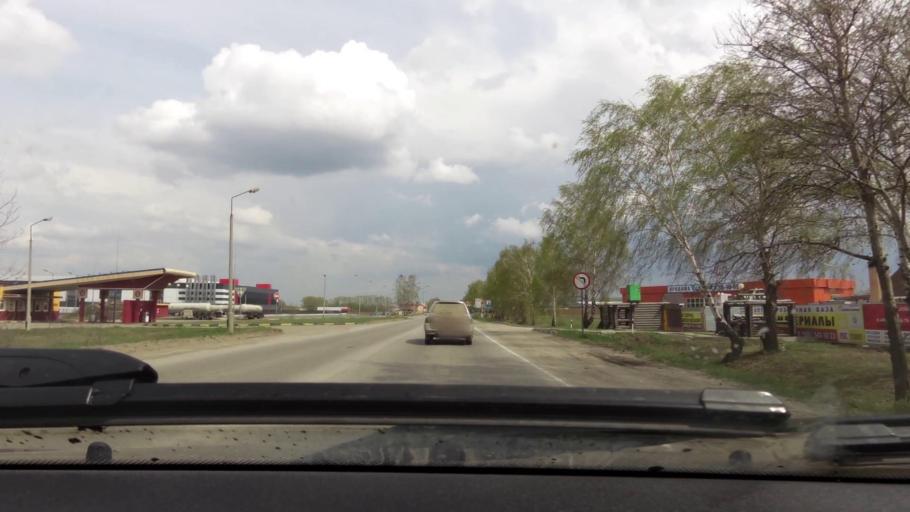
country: RU
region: Rjazan
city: Bagramovo
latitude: 54.7297
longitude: 39.4702
